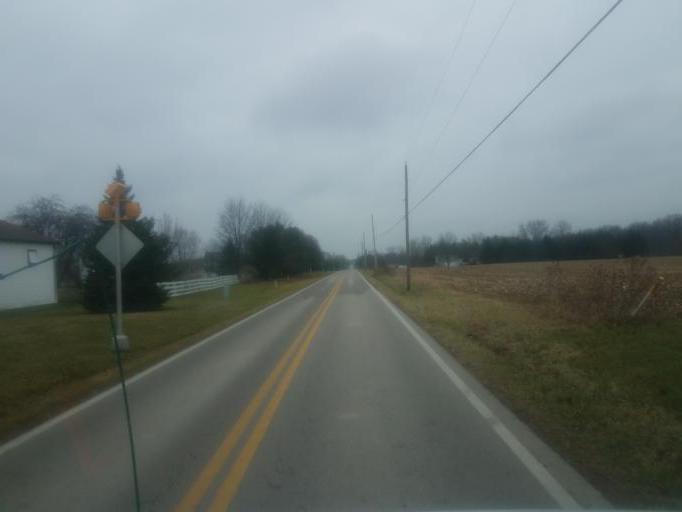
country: US
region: Ohio
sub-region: Delaware County
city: Sunbury
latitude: 40.2169
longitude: -82.9158
